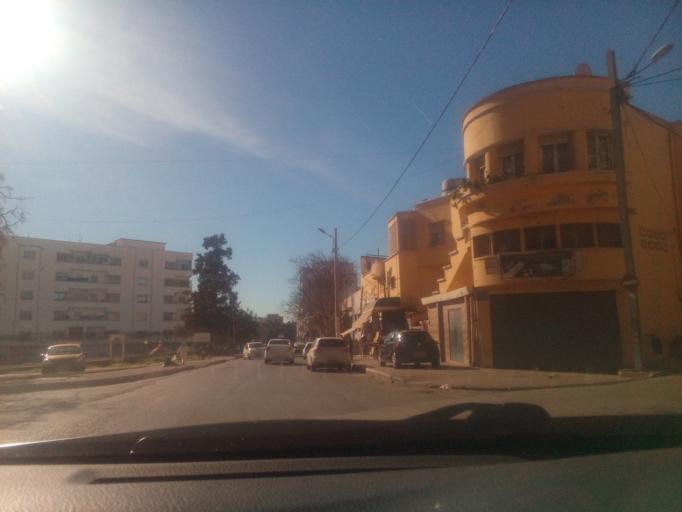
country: DZ
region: Oran
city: Oran
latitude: 35.7040
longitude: -0.6067
